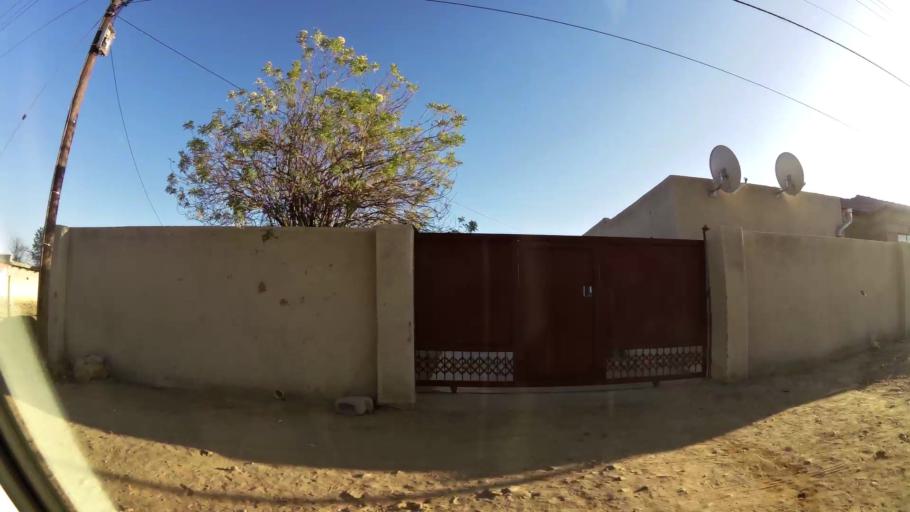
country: ZA
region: Limpopo
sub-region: Capricorn District Municipality
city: Polokwane
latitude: -23.8401
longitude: 29.3613
